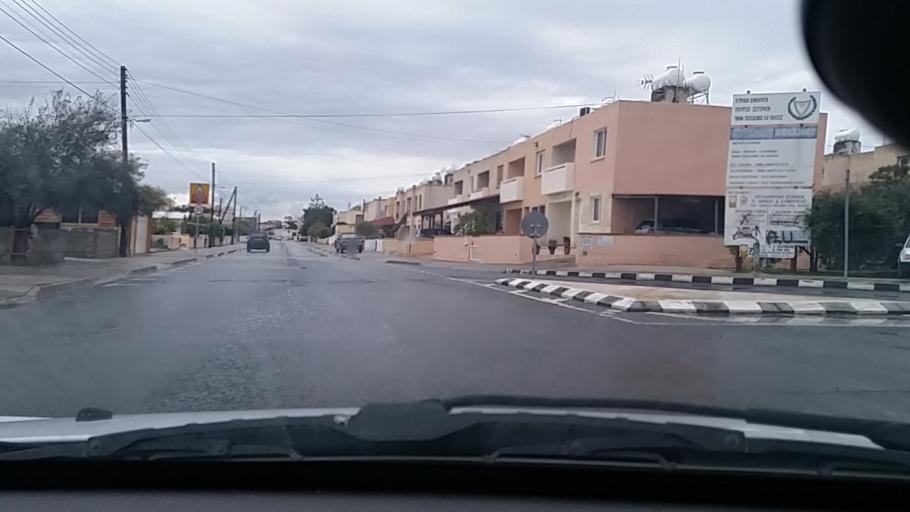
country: CY
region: Larnaka
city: Livadia
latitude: 34.9379
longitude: 33.6188
